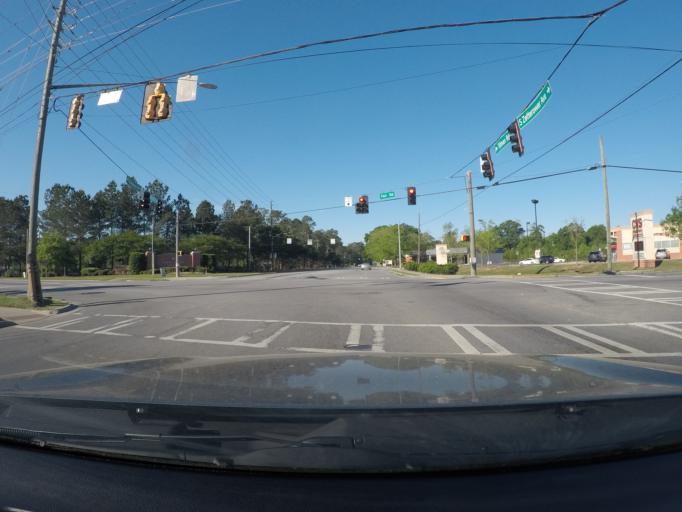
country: US
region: Georgia
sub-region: Bulloch County
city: Statesboro
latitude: 32.4348
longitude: -81.7821
